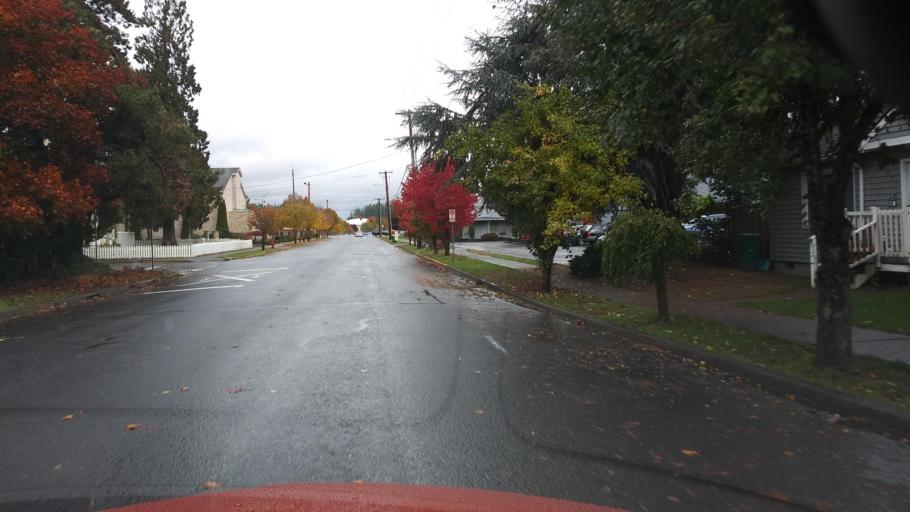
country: US
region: Oregon
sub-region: Washington County
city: Cornelius
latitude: 45.5181
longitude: -123.0758
